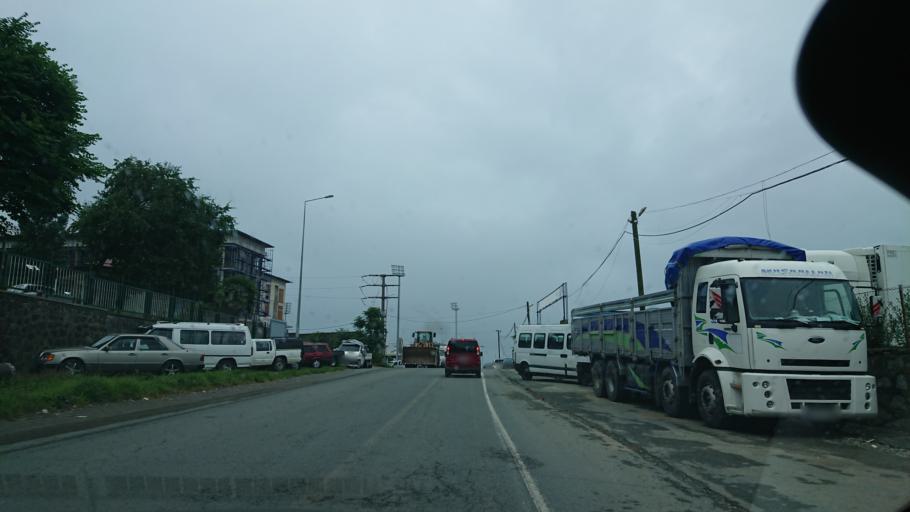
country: TR
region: Rize
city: Gundogdu
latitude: 41.0400
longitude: 40.5758
